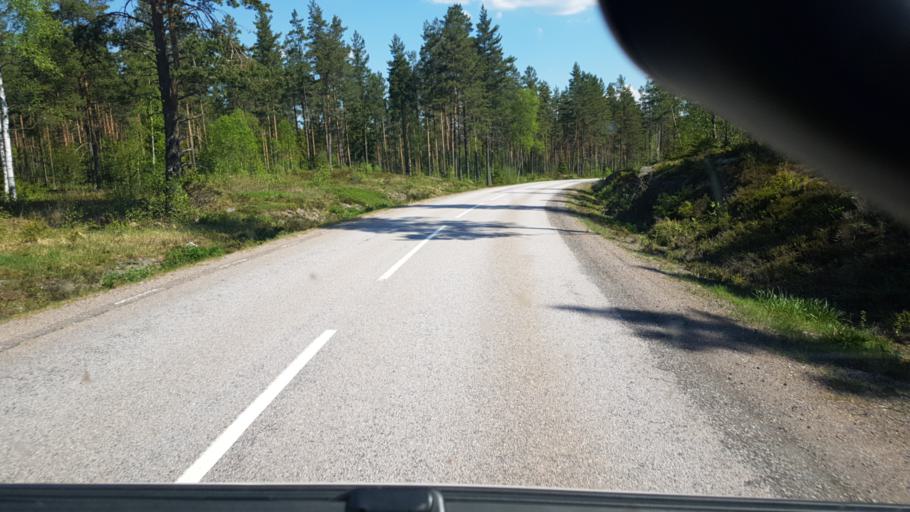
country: SE
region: Vaermland
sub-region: Arjangs Kommun
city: Arjaeng
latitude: 59.5637
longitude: 12.1841
